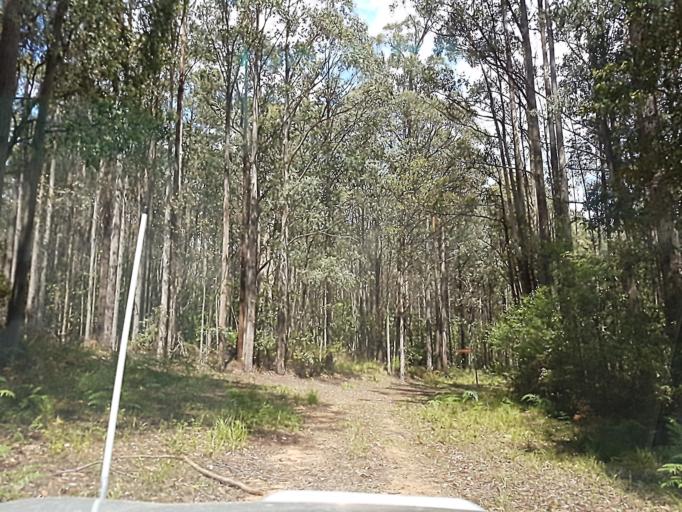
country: AU
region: Victoria
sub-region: East Gippsland
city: Lakes Entrance
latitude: -37.3288
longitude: 148.3251
